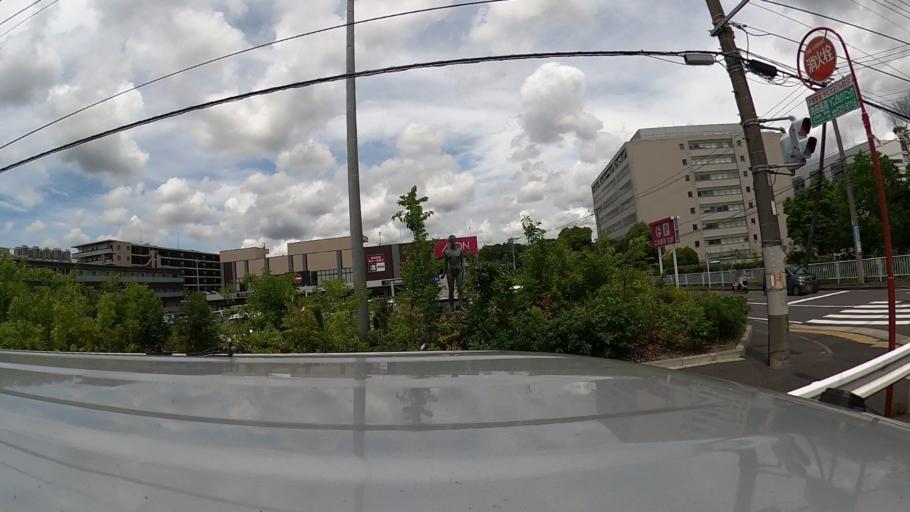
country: JP
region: Kanagawa
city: Fujisawa
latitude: 35.4091
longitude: 139.5393
